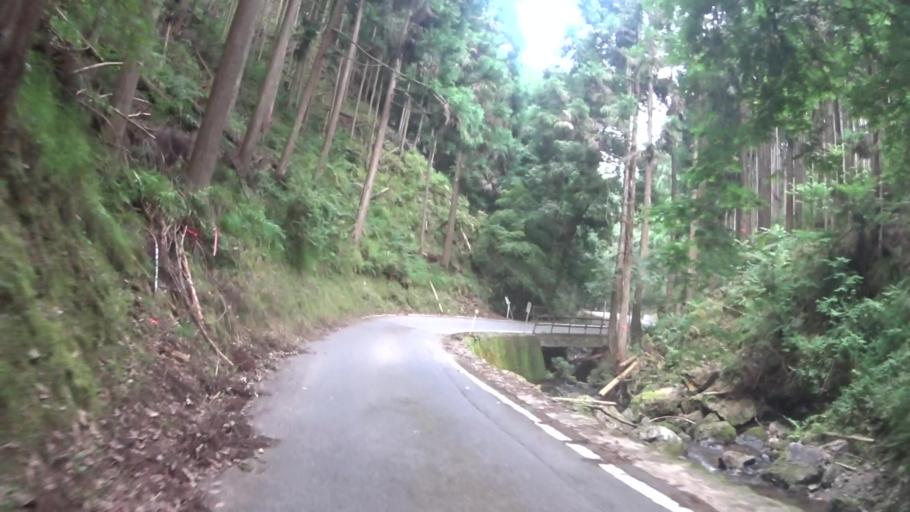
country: JP
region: Kyoto
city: Kameoka
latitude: 35.1562
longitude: 135.5733
